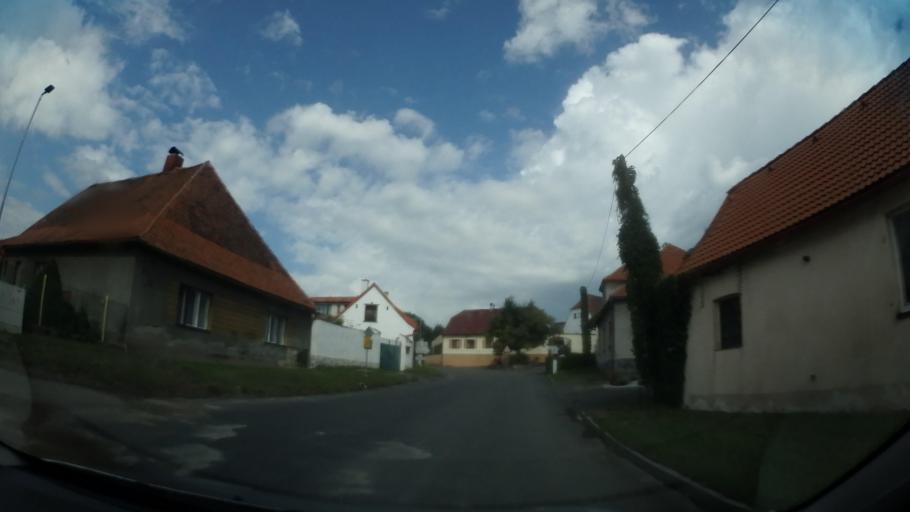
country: CZ
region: Plzensky
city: Horazd'ovice
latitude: 49.2669
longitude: 13.6307
